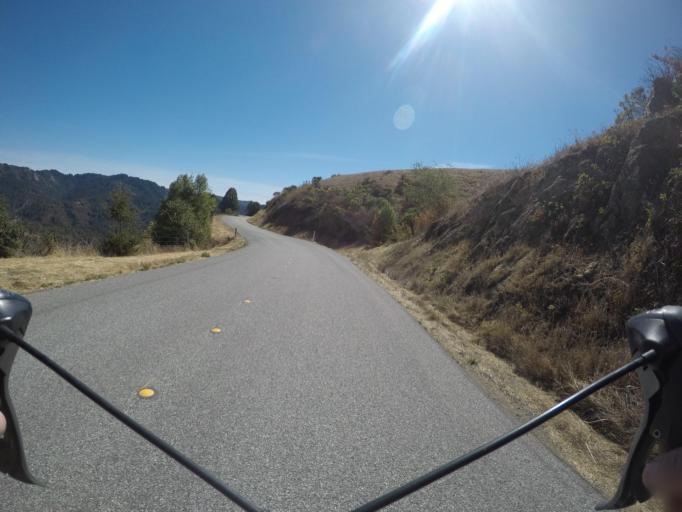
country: US
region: California
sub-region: San Mateo County
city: Portola Valley
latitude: 37.2962
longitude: -122.2067
